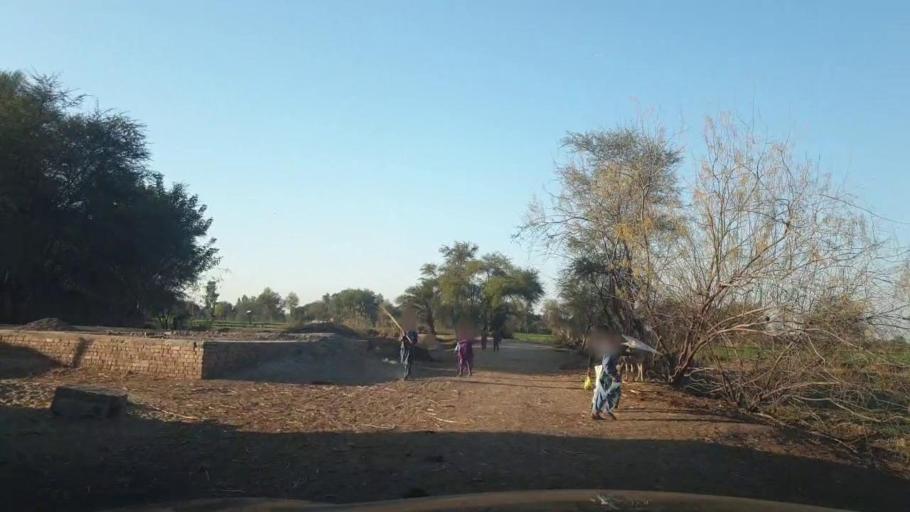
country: PK
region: Sindh
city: Mirpur Mathelo
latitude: 28.0051
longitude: 69.4651
